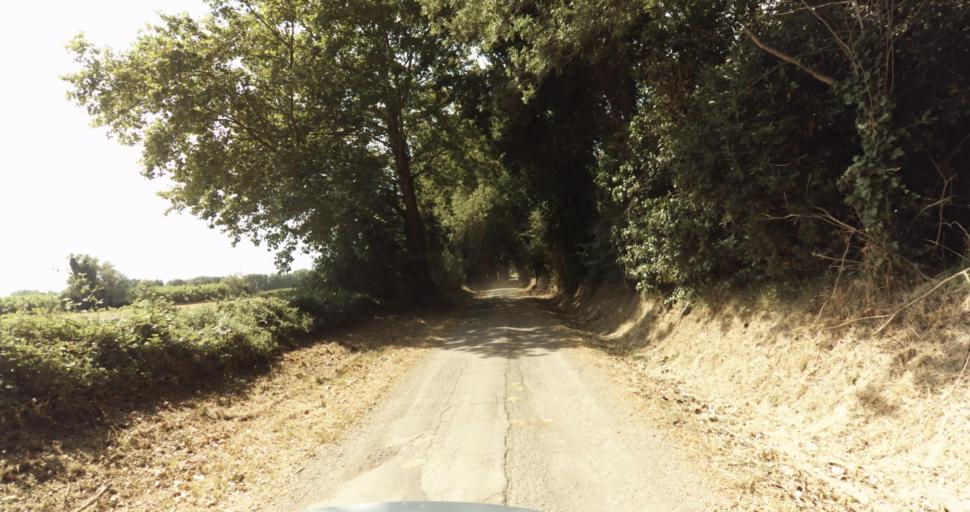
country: FR
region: Languedoc-Roussillon
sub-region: Departement des Pyrenees-Orientales
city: Latour-Bas-Elne
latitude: 42.6043
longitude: 3.0262
